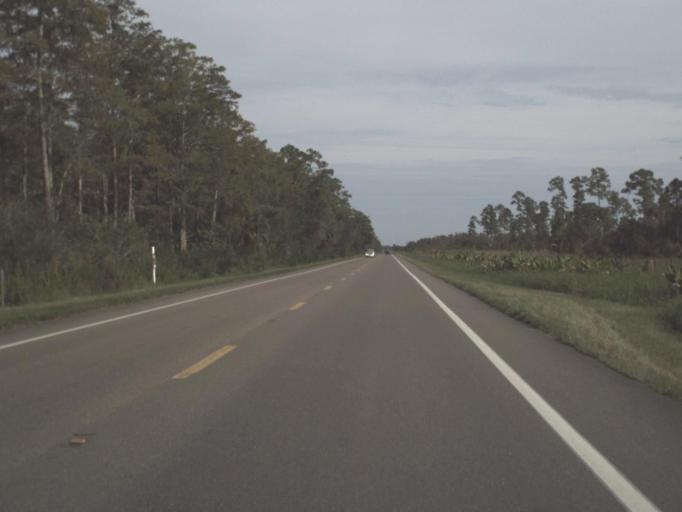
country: US
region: Florida
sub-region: Lee County
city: Olga
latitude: 26.9287
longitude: -81.7606
